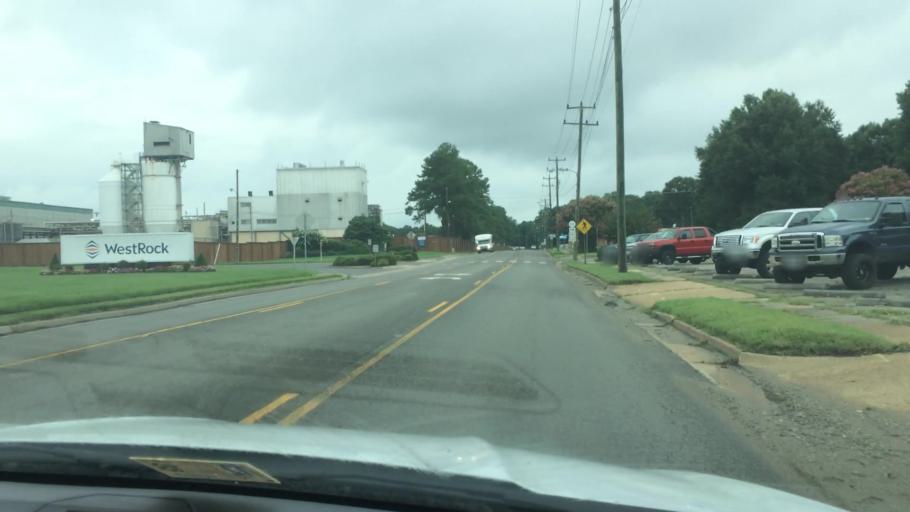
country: US
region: Virginia
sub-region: King William County
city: West Point
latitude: 37.5400
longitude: -76.8009
